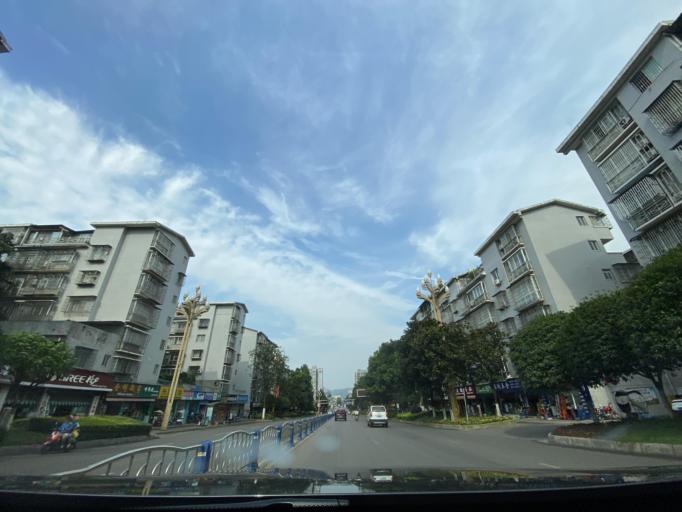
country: CN
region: Sichuan
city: Fuji
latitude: 29.1529
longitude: 105.3582
